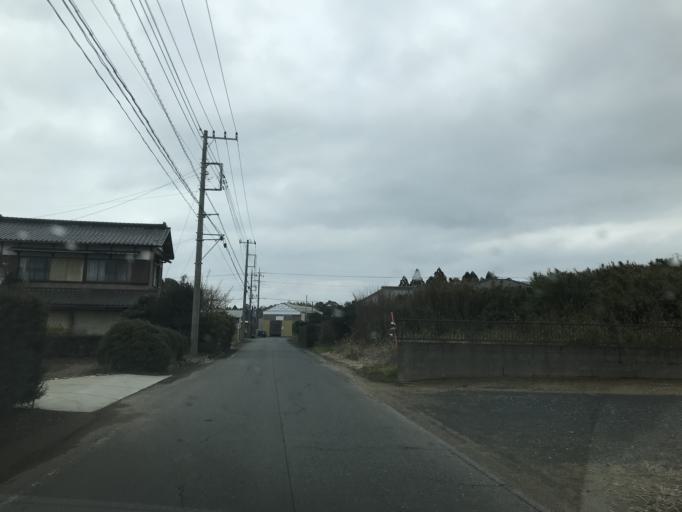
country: JP
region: Chiba
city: Sawara
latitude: 35.8597
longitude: 140.5504
